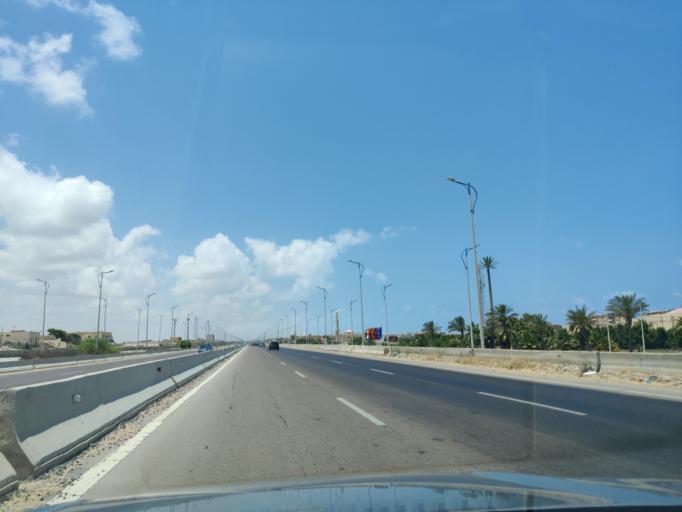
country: EG
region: Muhafazat Matruh
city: Al `Alamayn
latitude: 30.9081
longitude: 29.4323
